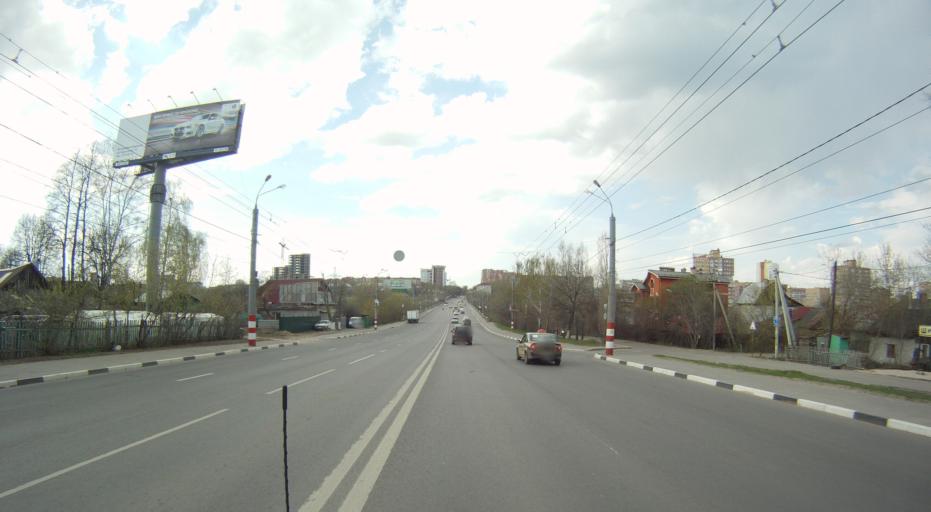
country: RU
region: Nizjnij Novgorod
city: Nizhniy Novgorod
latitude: 56.3039
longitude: 44.0281
